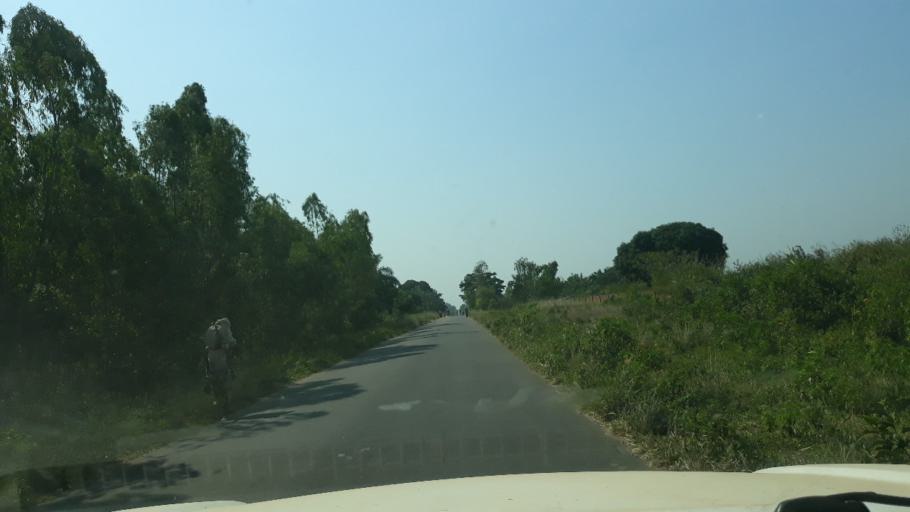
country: CD
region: South Kivu
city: Uvira
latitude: -3.3025
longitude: 29.1602
